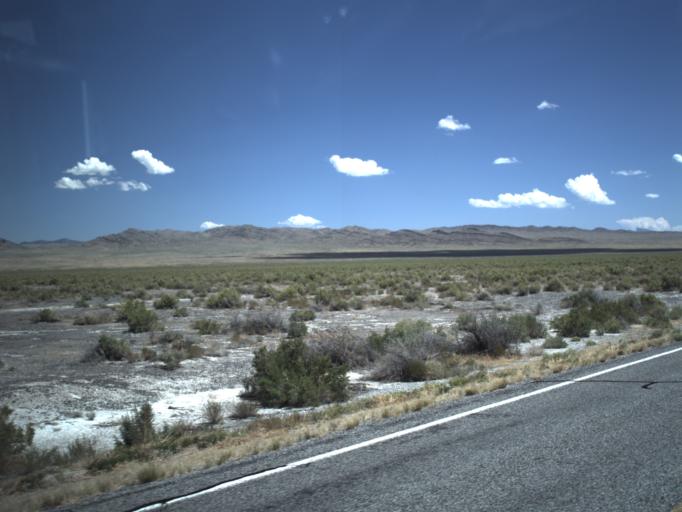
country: US
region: Nevada
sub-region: White Pine County
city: McGill
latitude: 39.0481
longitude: -113.9313
